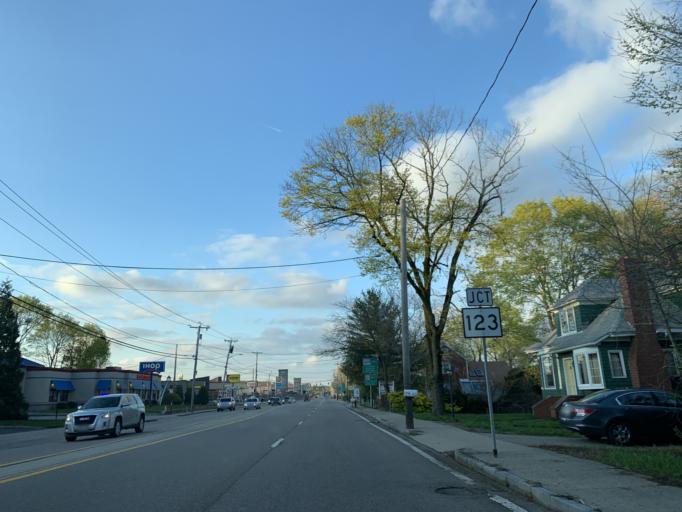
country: US
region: Rhode Island
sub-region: Providence County
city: Valley Falls
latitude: 41.9180
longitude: -71.3593
